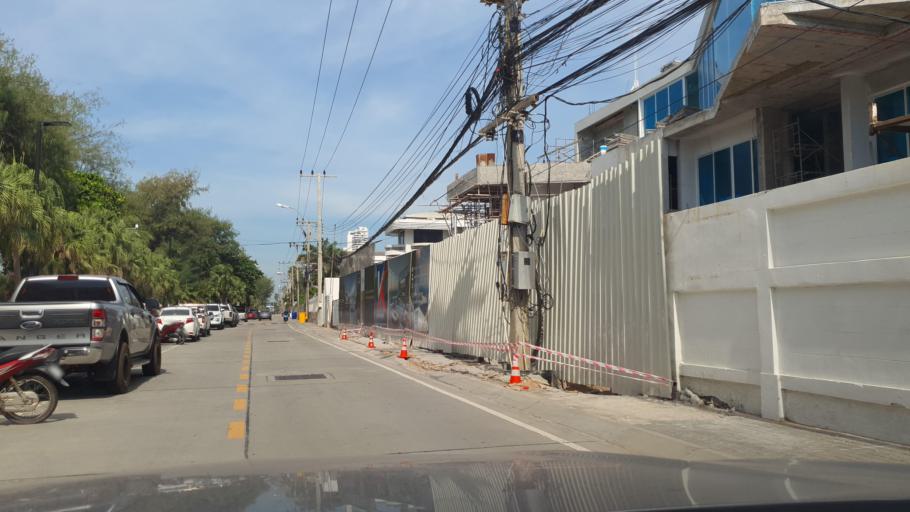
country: TH
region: Chon Buri
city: Phatthaya
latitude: 12.9009
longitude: 100.8646
